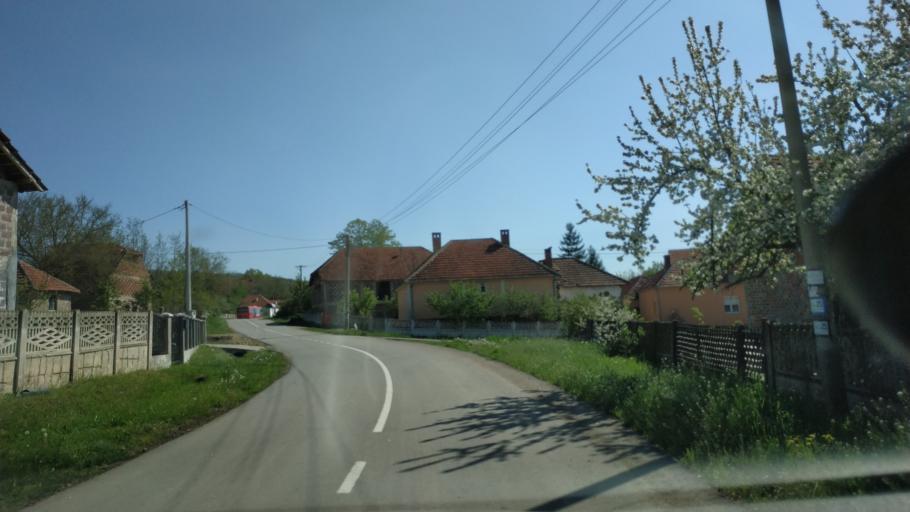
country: RS
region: Central Serbia
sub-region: Nisavski Okrug
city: Nis
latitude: 43.4652
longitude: 21.8619
